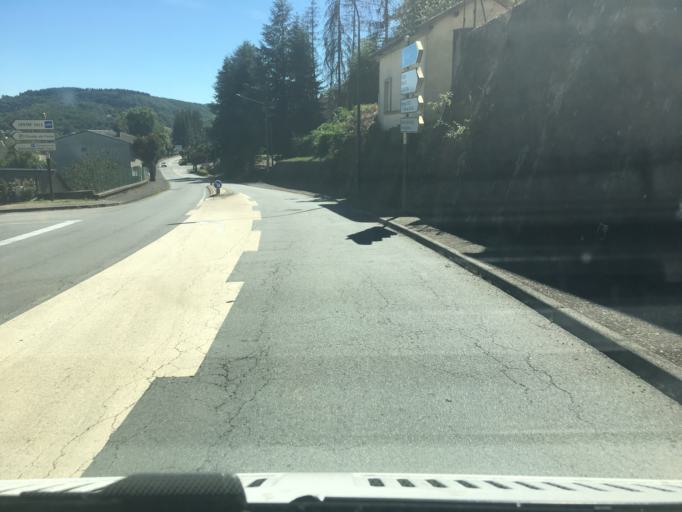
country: FR
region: Limousin
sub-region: Departement de la Correze
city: Bort-les-Orgues
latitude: 45.4022
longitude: 2.4939
